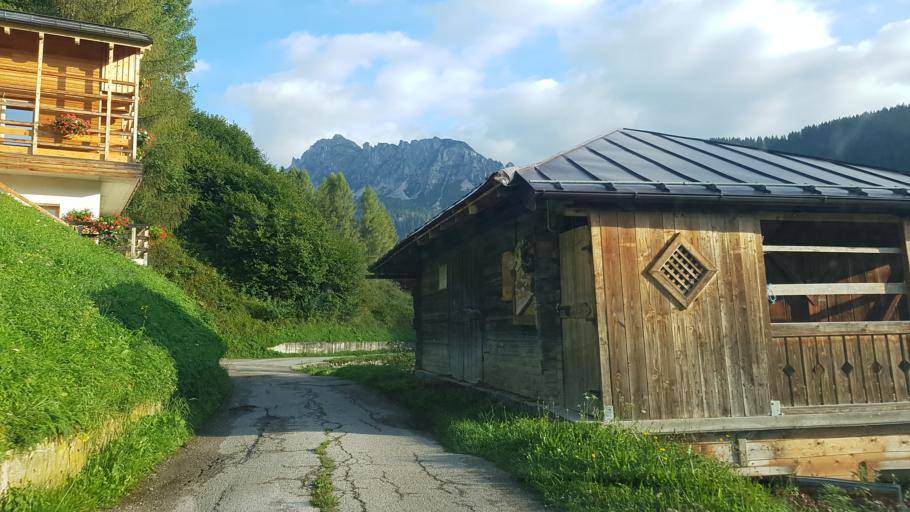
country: IT
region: Veneto
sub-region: Provincia di Belluno
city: San Pietro di Cadore
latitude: 46.5854
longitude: 12.5815
